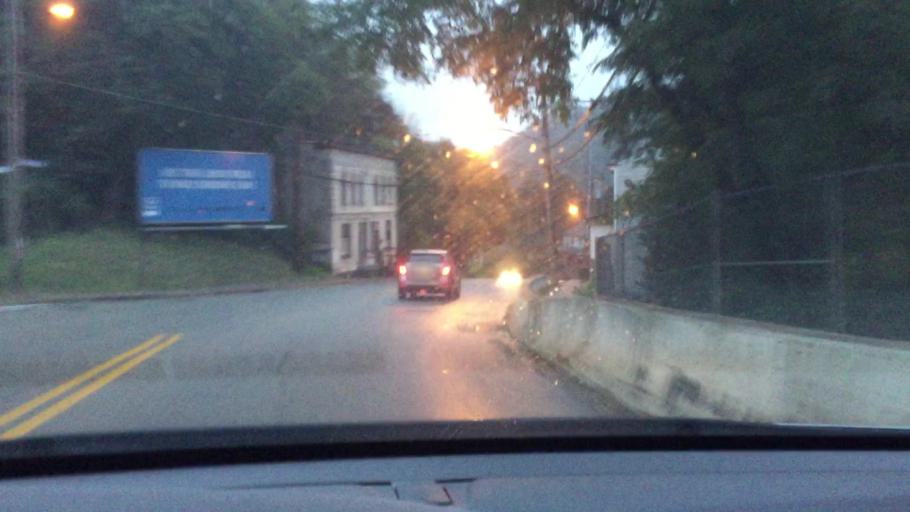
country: US
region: Pennsylvania
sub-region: Allegheny County
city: Crafton
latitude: 40.4412
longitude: -80.0378
